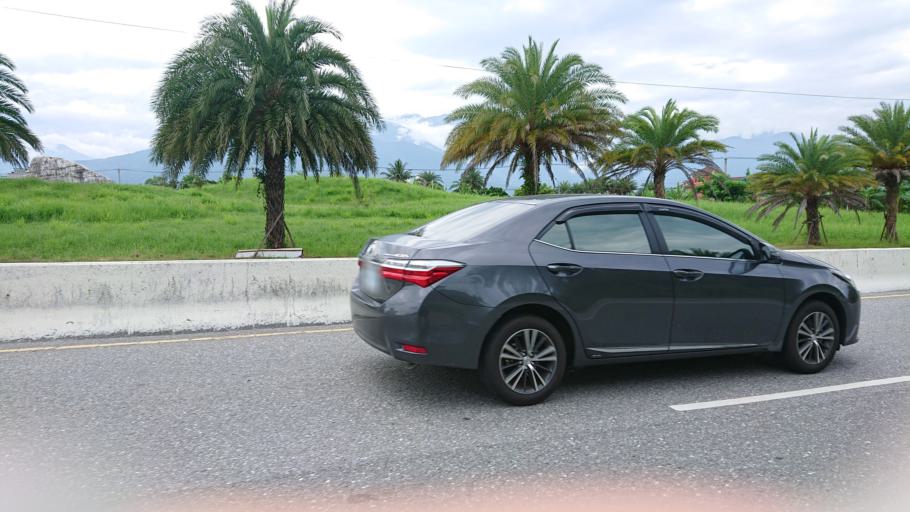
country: TW
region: Taiwan
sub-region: Hualien
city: Hualian
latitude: 23.9404
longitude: 121.5946
